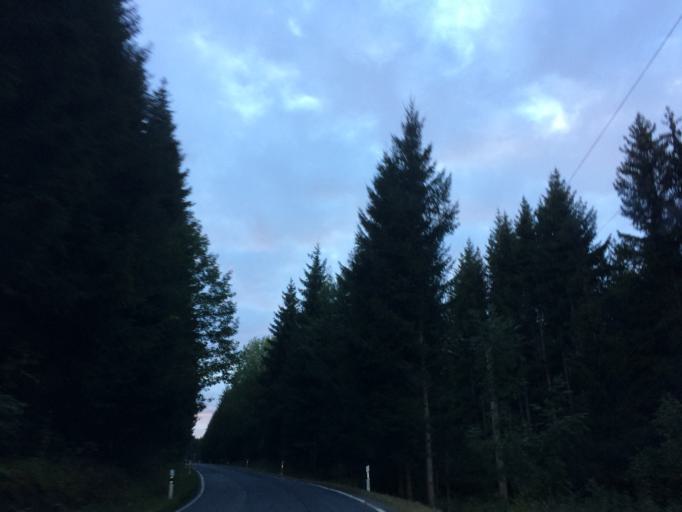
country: DE
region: Thuringia
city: Moxa
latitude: 50.6418
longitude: 11.6131
